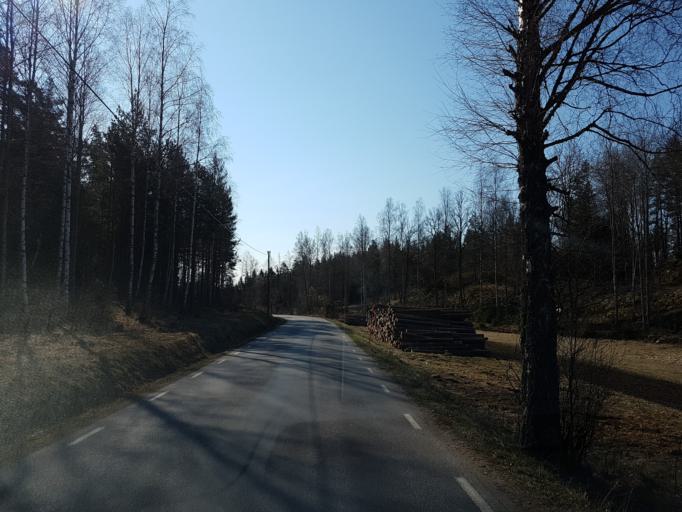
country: SE
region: Kalmar
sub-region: Vasterviks Kommun
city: Overum
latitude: 58.1543
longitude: 16.2266
